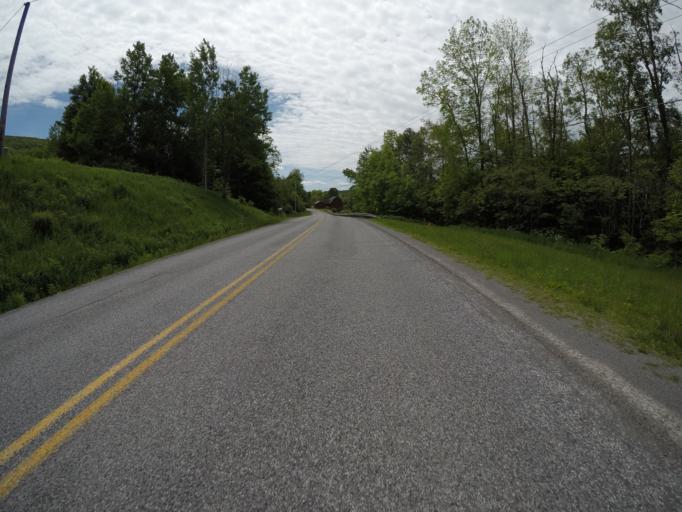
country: US
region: New York
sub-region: Delaware County
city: Stamford
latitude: 42.2333
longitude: -74.5598
